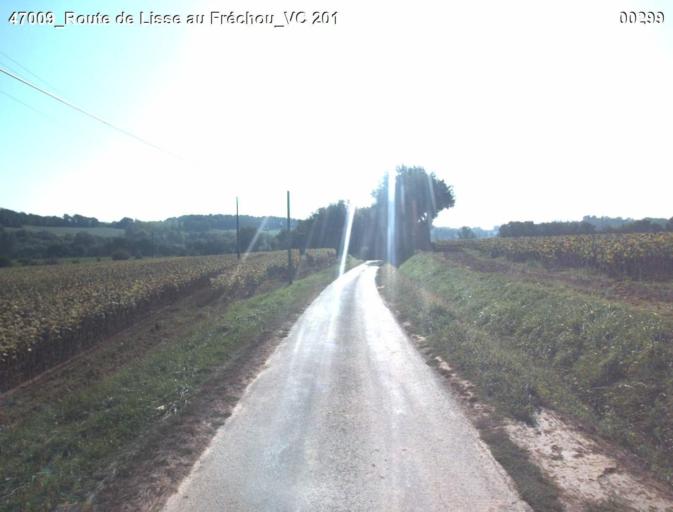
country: FR
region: Aquitaine
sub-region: Departement du Lot-et-Garonne
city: Nerac
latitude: 44.0937
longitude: 0.3070
